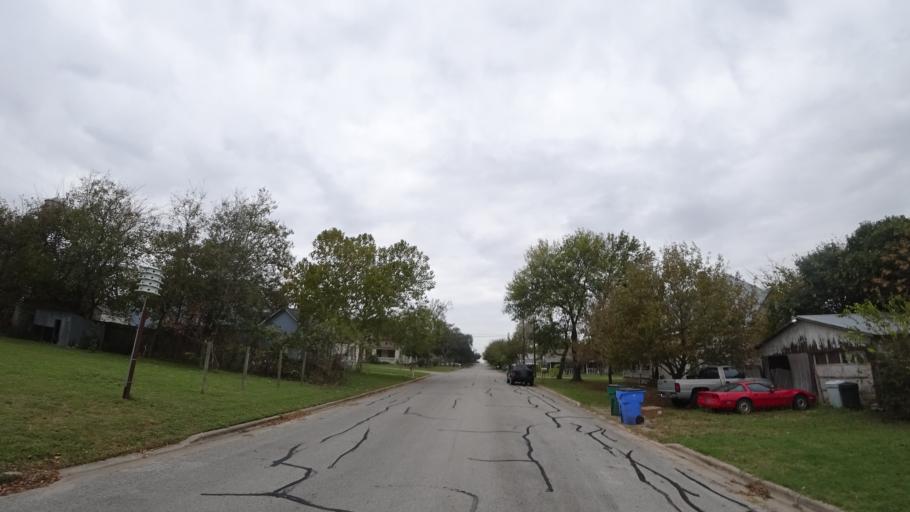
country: US
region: Texas
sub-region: Travis County
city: Pflugerville
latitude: 30.4385
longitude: -97.6223
